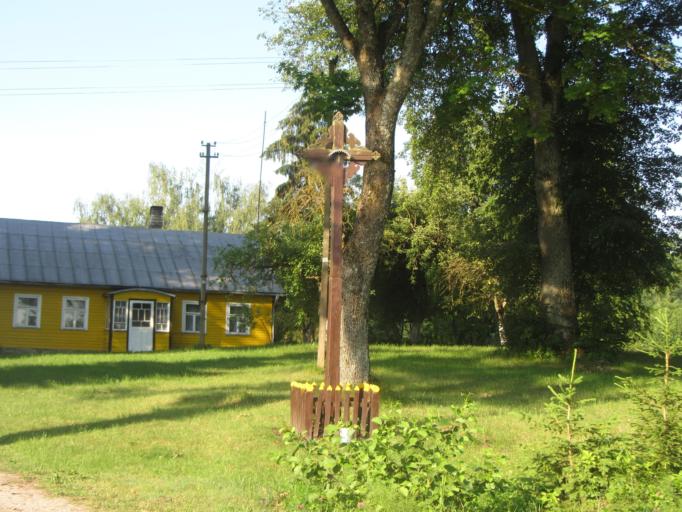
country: LT
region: Alytaus apskritis
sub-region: Alytus
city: Alytus
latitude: 54.2992
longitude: 23.9580
